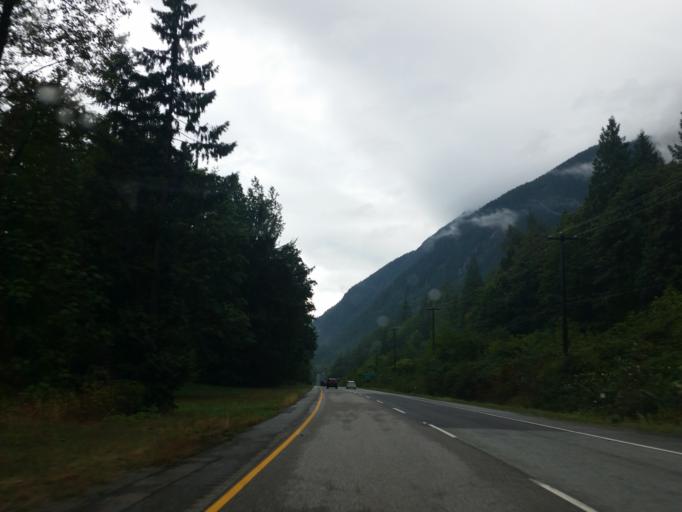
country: CA
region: British Columbia
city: Agassiz
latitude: 49.2293
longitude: -121.6830
